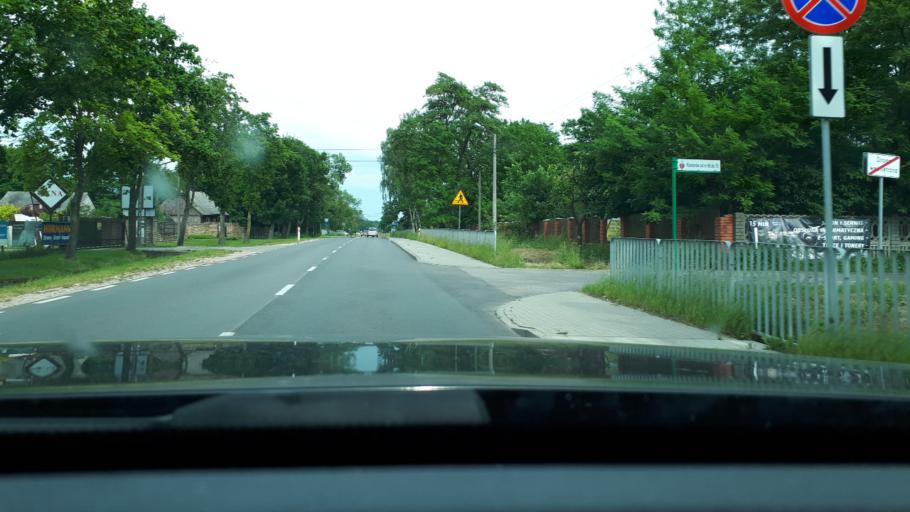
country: PL
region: Masovian Voivodeship
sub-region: Powiat warszawski zachodni
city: Kampinos
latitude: 52.2698
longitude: 20.4286
